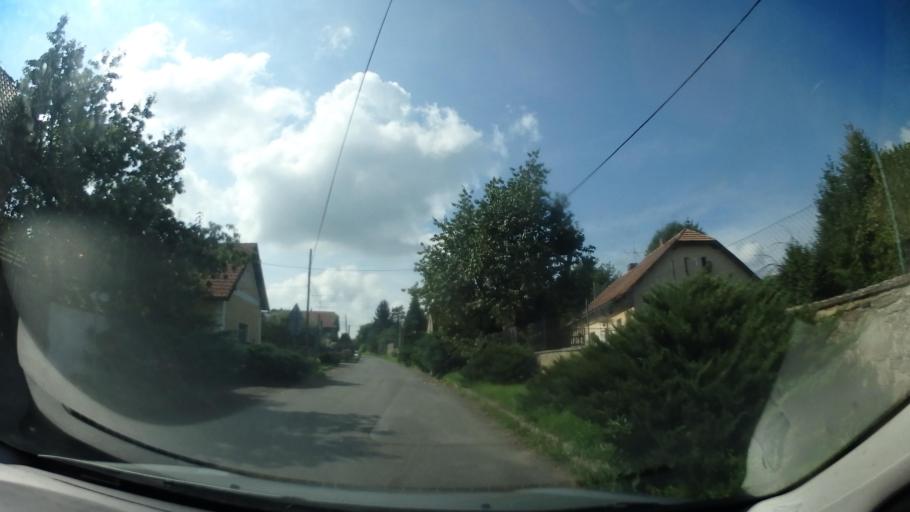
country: CZ
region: Central Bohemia
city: Sedlcany
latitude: 49.7030
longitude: 14.3463
